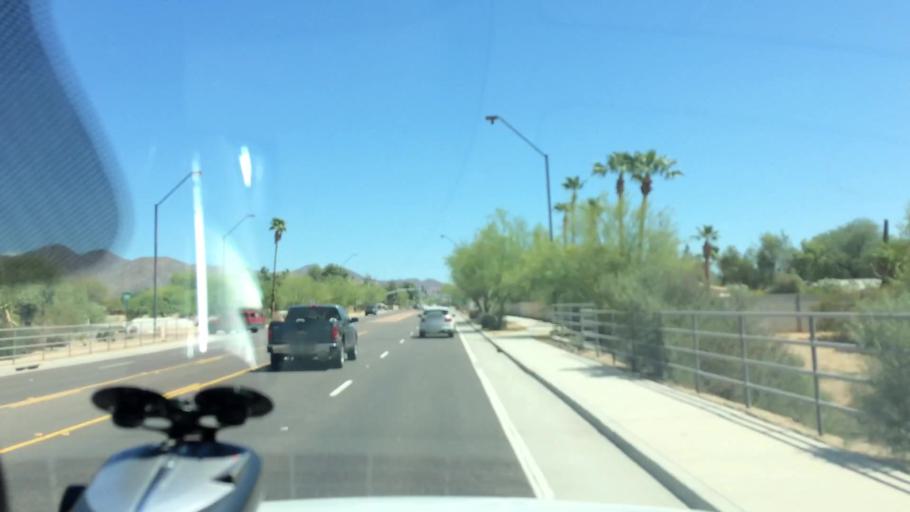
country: US
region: Arizona
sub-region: Maricopa County
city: Scottsdale
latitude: 33.5970
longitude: -111.8813
